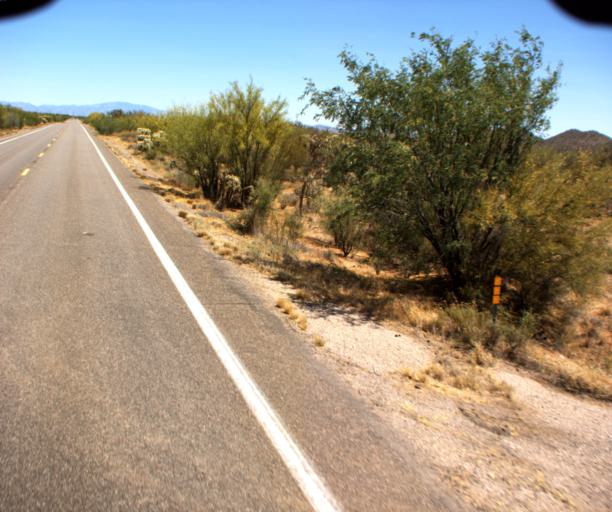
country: US
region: Arizona
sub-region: Pima County
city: Marana
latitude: 32.7575
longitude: -111.1423
